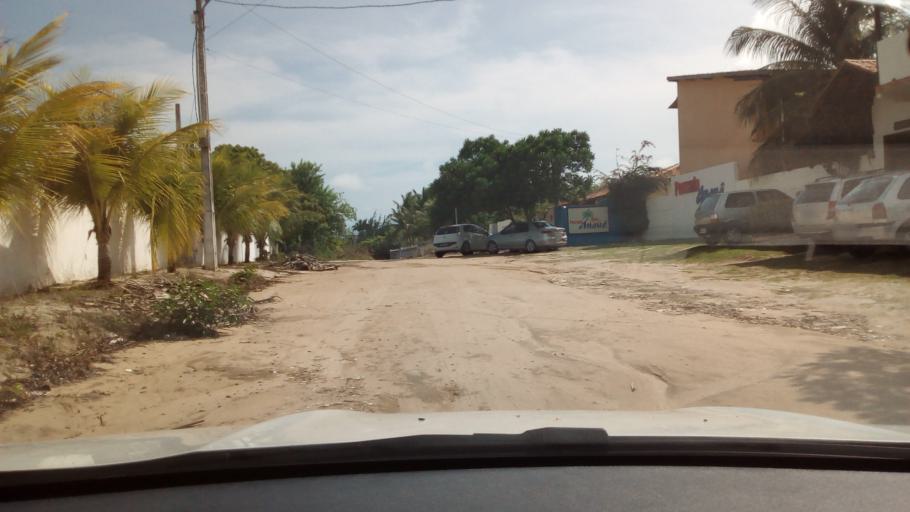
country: BR
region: Paraiba
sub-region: Conde
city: Conde
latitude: -7.2960
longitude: -34.8028
